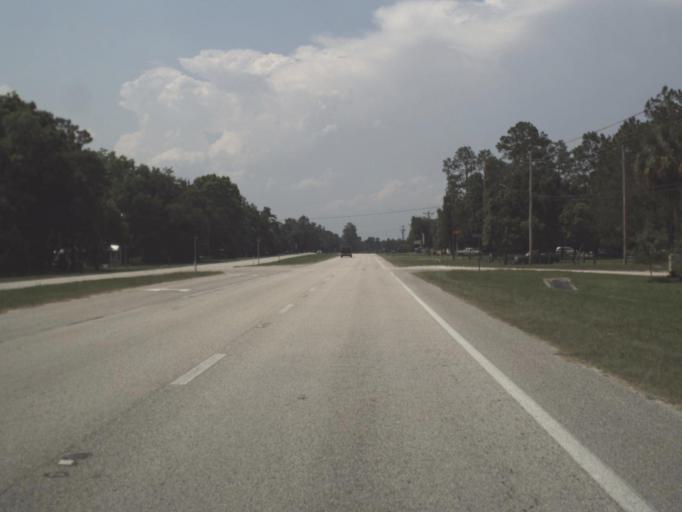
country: US
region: Florida
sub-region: Clay County
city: Green Cove Springs
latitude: 29.9283
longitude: -81.6861
